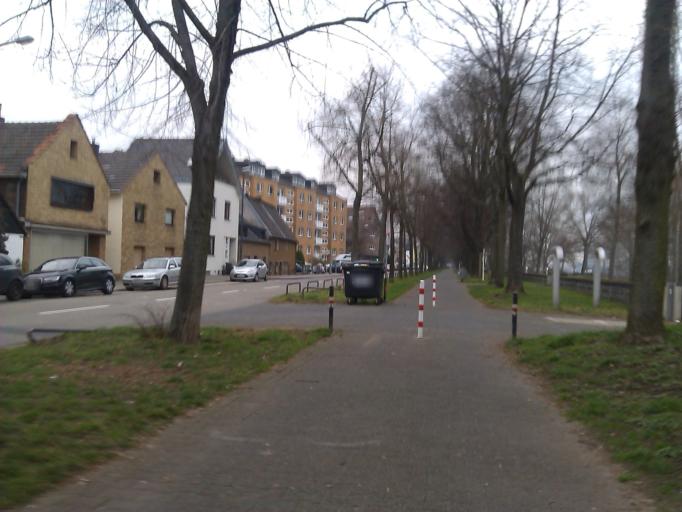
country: DE
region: North Rhine-Westphalia
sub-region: Regierungsbezirk Koln
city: Riehl
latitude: 50.9878
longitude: 6.9655
